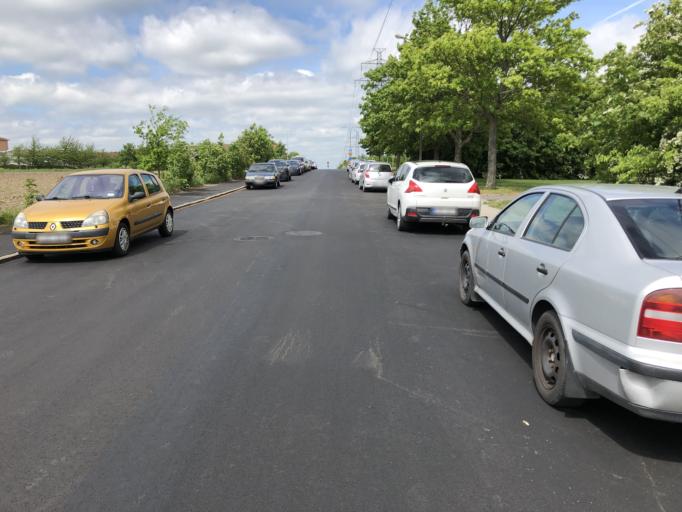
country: SE
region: Skane
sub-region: Lunds Kommun
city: Lund
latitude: 55.7022
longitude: 13.1614
